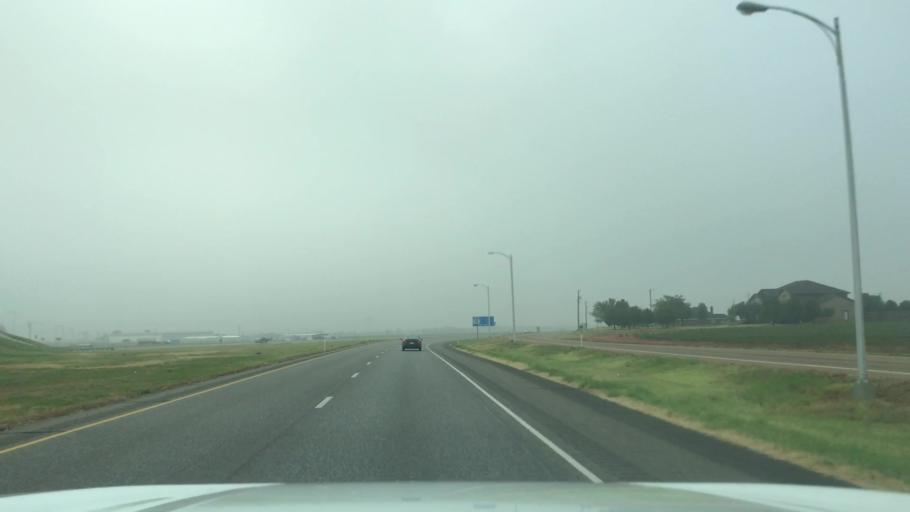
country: US
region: Texas
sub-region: Lubbock County
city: Slaton
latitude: 33.4585
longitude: -101.6692
